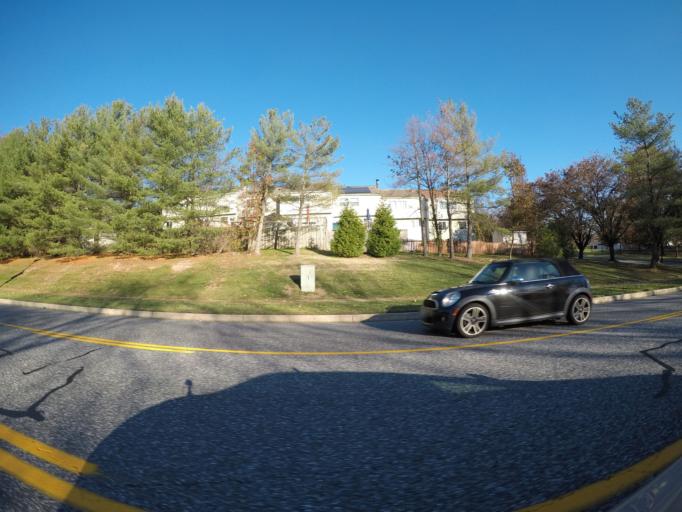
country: US
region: Maryland
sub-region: Harford County
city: Bel Air South
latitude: 39.4740
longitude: -76.3007
